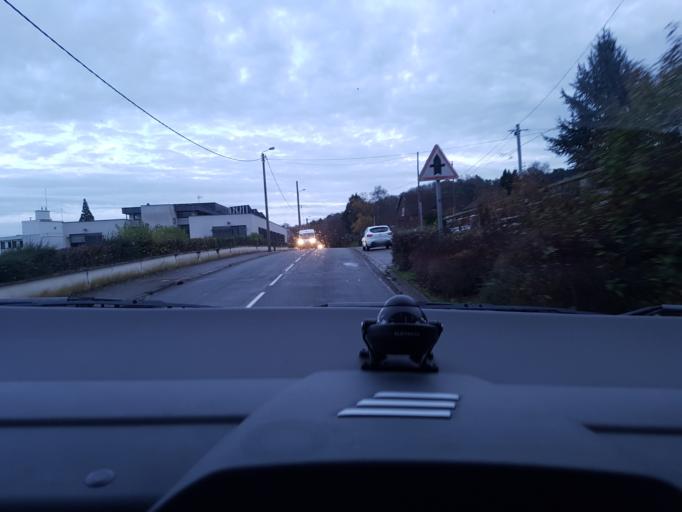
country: FR
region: Picardie
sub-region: Departement de la Somme
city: Poix-de-Picardie
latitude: 49.7755
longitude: 1.9775
